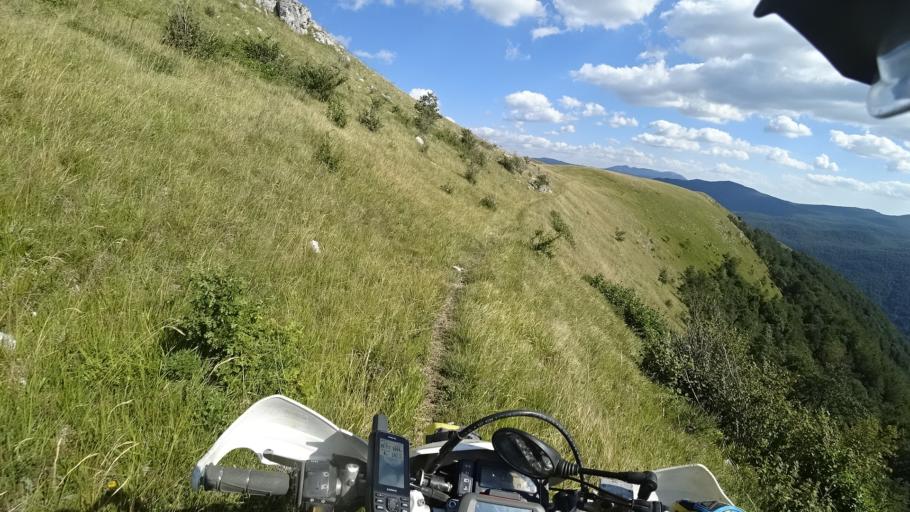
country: HR
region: Zadarska
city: Gracac
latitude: 44.3792
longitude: 16.0507
